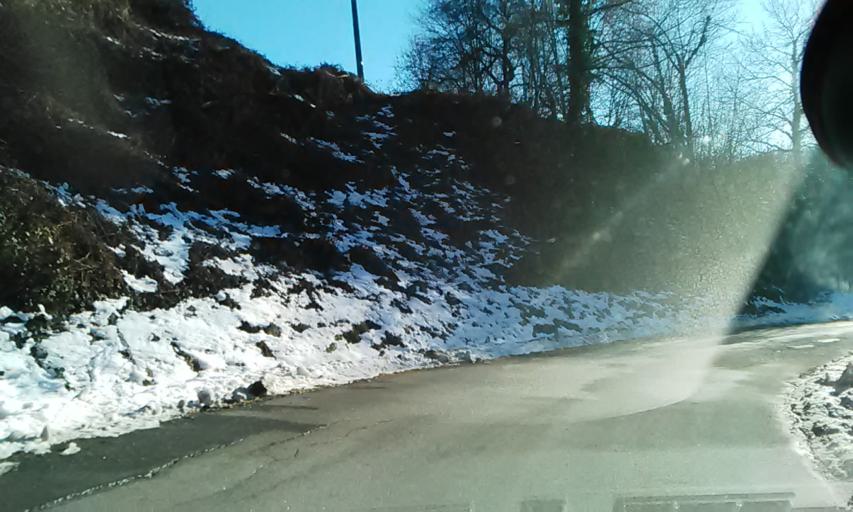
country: IT
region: Piedmont
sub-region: Provincia di Vercelli
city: Cellio
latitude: 45.7572
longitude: 8.3382
